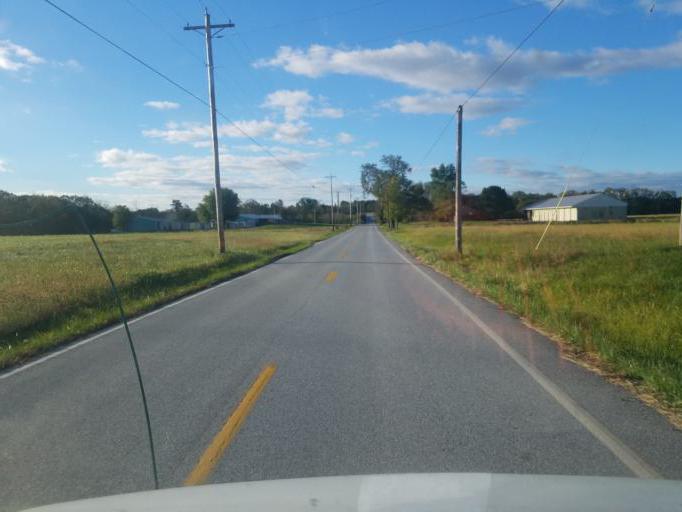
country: US
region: Pennsylvania
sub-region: Adams County
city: Gettysburg
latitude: 39.8792
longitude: -77.2301
